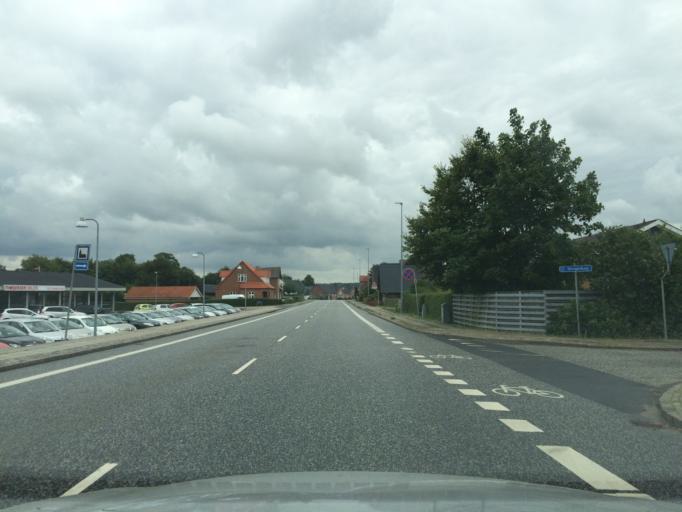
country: DK
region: Central Jutland
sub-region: Silkeborg Kommune
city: Svejbaek
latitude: 56.1919
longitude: 9.6912
